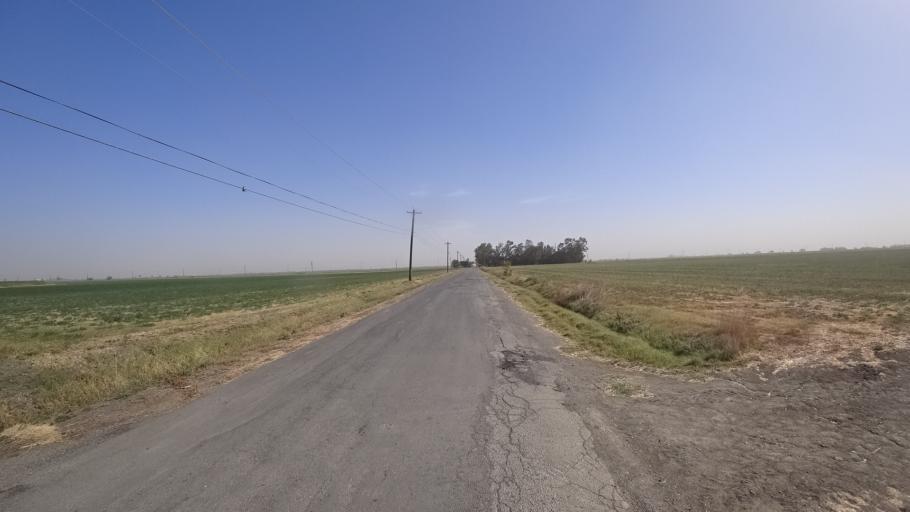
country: US
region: California
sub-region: Yolo County
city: Davis
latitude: 38.5749
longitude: -121.6797
